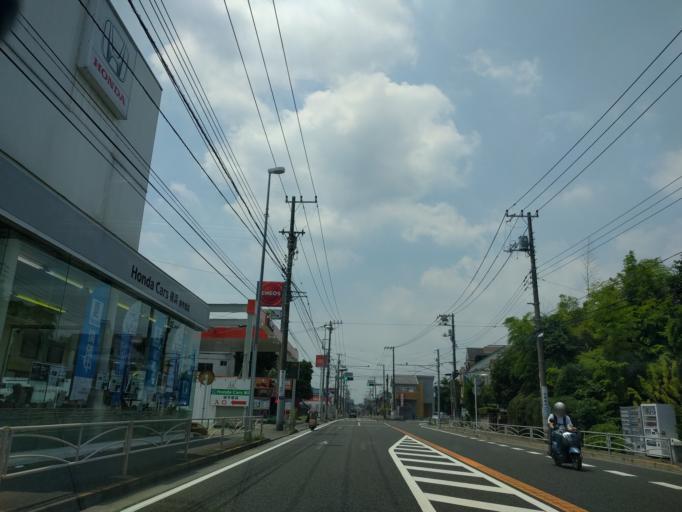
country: JP
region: Kanagawa
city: Minami-rinkan
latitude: 35.4795
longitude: 139.5368
